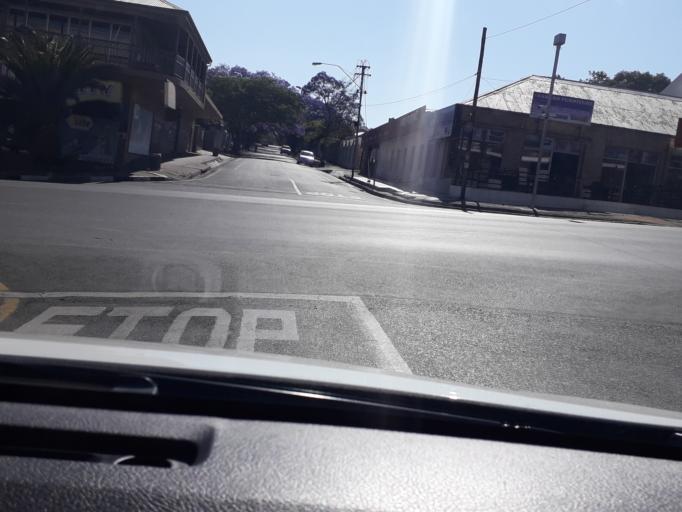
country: ZA
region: Gauteng
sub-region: City of Johannesburg Metropolitan Municipality
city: Johannesburg
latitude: -26.1774
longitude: 28.0009
